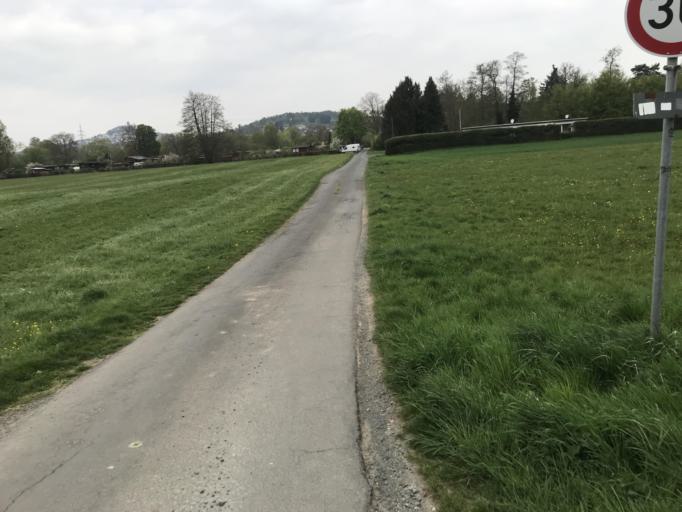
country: DE
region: Hesse
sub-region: Regierungsbezirk Giessen
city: Giessen
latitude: 50.6098
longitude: 8.6722
